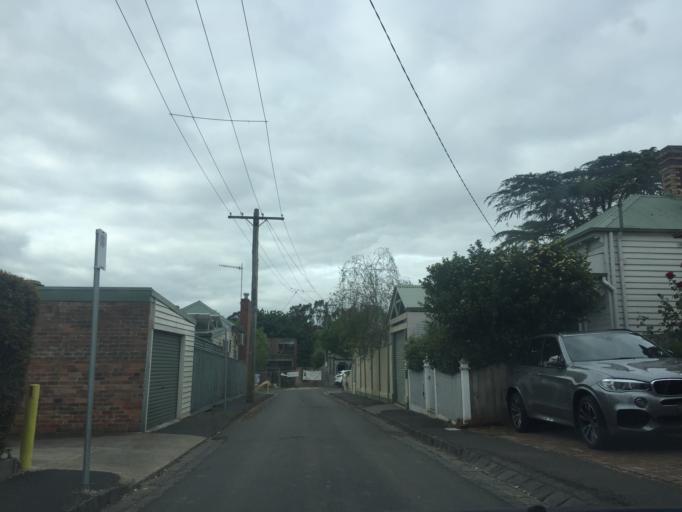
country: AU
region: Victoria
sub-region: Boroondara
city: Hawthorn East
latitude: -37.8222
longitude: 145.0522
